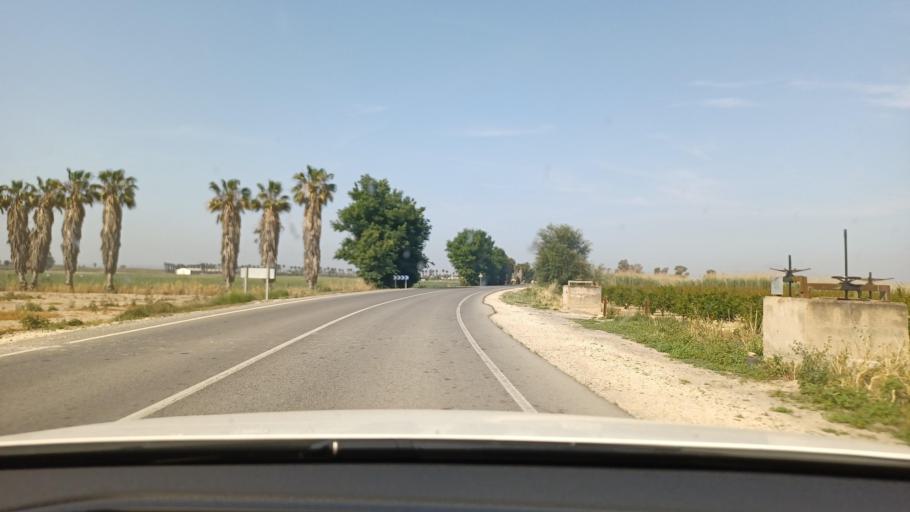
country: ES
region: Valencia
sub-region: Provincia de Alicante
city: Daya Vieja
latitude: 38.1495
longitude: -0.7180
